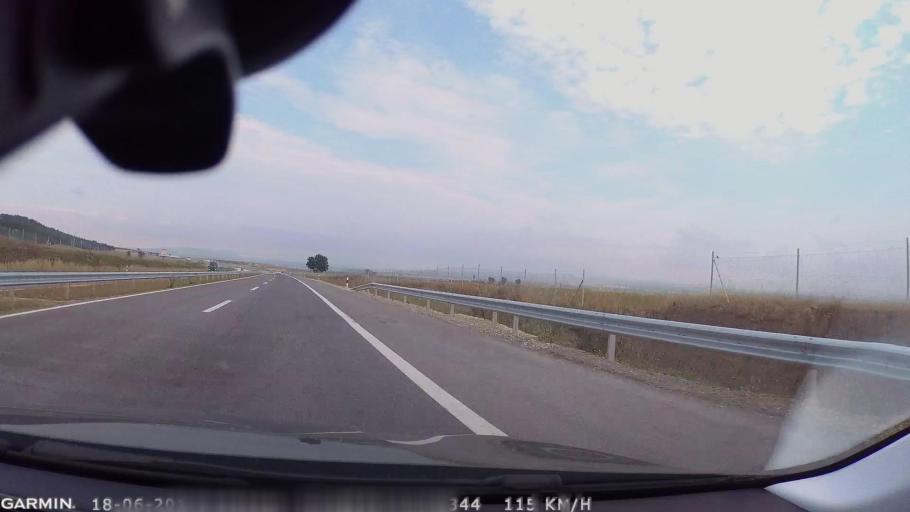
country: MK
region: Sveti Nikole
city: Sveti Nikole
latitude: 41.8078
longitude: 22.0625
